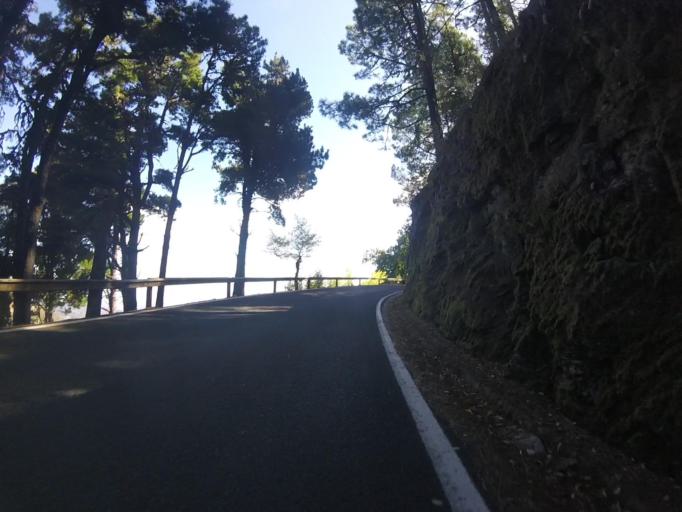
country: ES
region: Canary Islands
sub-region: Provincia de Las Palmas
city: Valleseco
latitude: 28.0169
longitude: -15.5837
